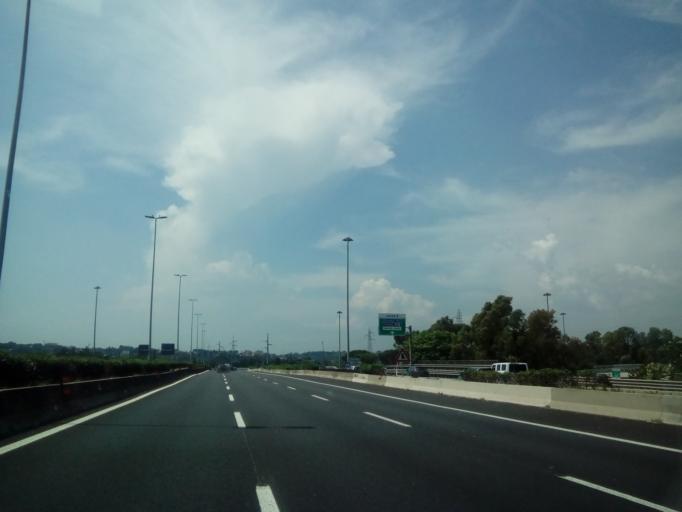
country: IT
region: Latium
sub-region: Citta metropolitana di Roma Capitale
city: Monte Caminetto
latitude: 41.9885
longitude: 12.5144
